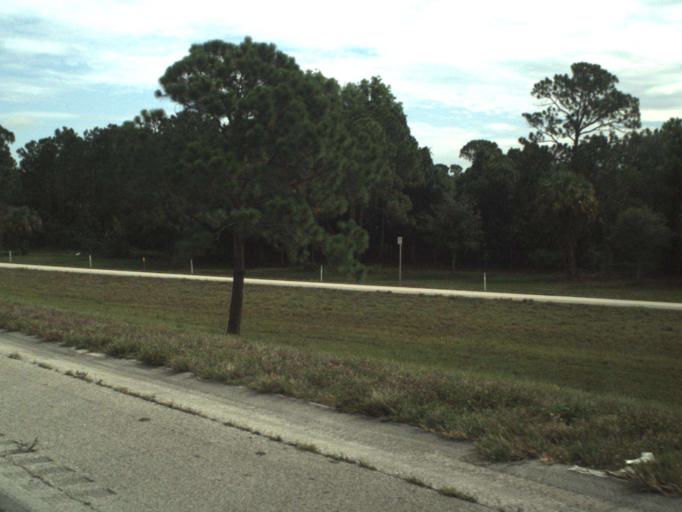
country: US
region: Florida
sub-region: Martin County
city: Palm City
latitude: 27.1641
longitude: -80.3903
